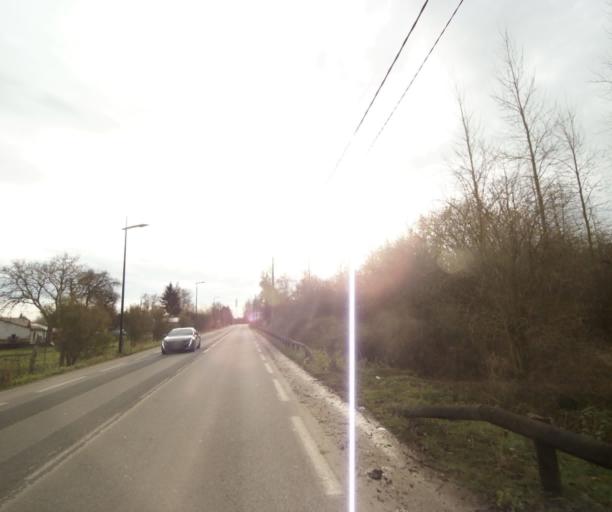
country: FR
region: Nord-Pas-de-Calais
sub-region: Departement du Nord
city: Fresnes-sur-Escaut
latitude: 50.4215
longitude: 3.5844
